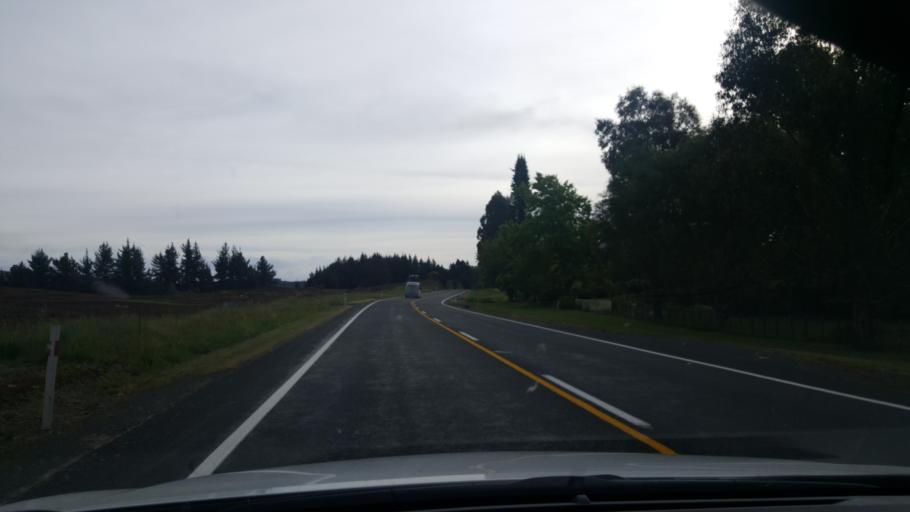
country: NZ
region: Waikato
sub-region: Taupo District
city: Taupo
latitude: -38.6129
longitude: 176.1180
